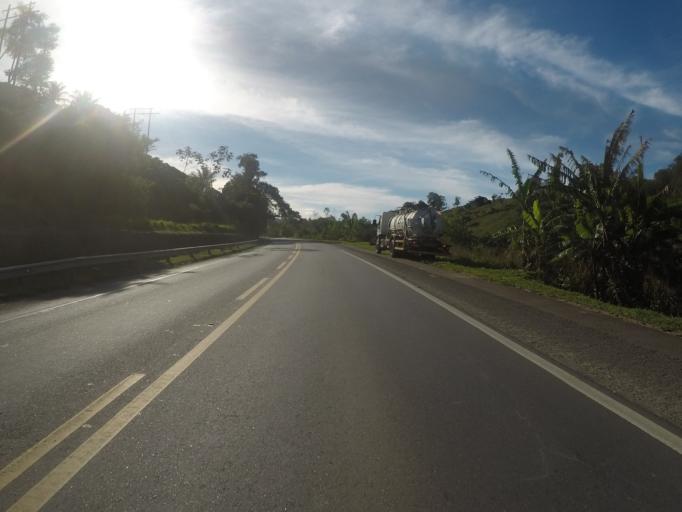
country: BR
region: Espirito Santo
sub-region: Fundao
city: Fundao
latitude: -19.8992
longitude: -40.4098
